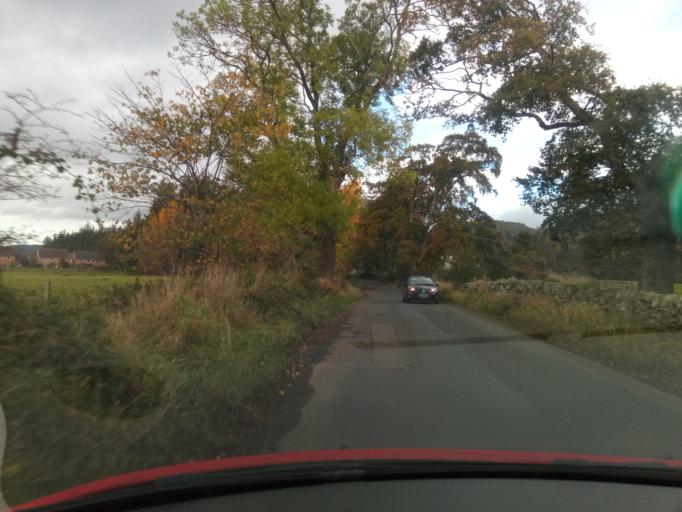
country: GB
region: Scotland
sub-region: The Scottish Borders
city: Peebles
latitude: 55.6440
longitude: -3.1650
